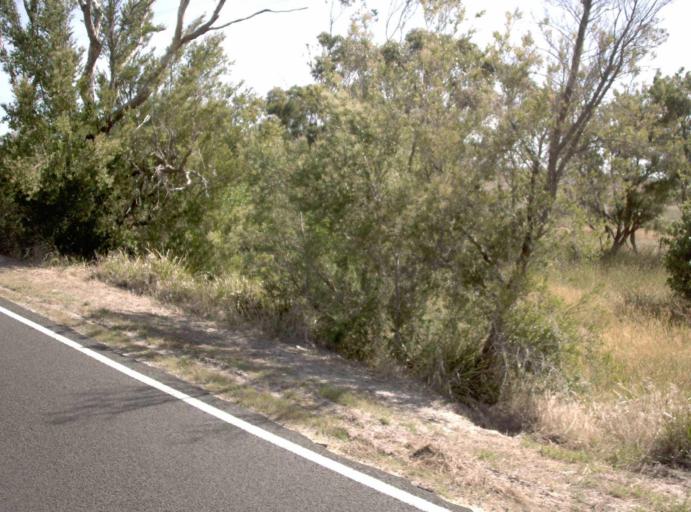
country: AU
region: Victoria
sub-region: Wellington
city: Sale
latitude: -38.3368
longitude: 147.1633
